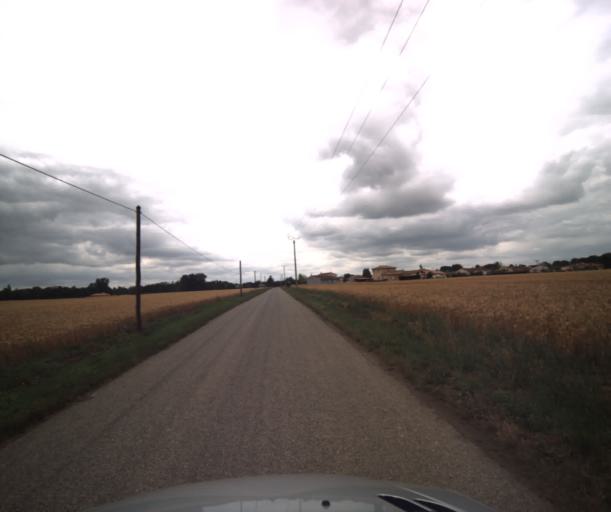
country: FR
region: Midi-Pyrenees
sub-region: Departement de la Haute-Garonne
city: Labarthe-sur-Leze
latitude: 43.4611
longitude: 1.4076
